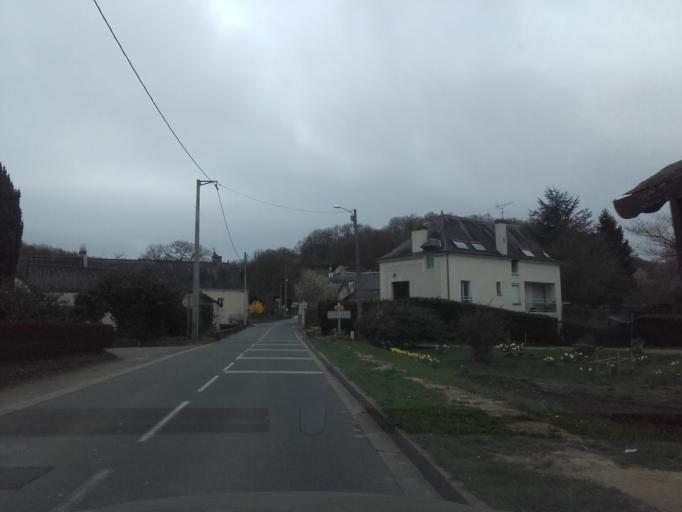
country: FR
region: Centre
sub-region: Departement d'Indre-et-Loire
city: Huismes
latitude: 47.2557
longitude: 0.3099
